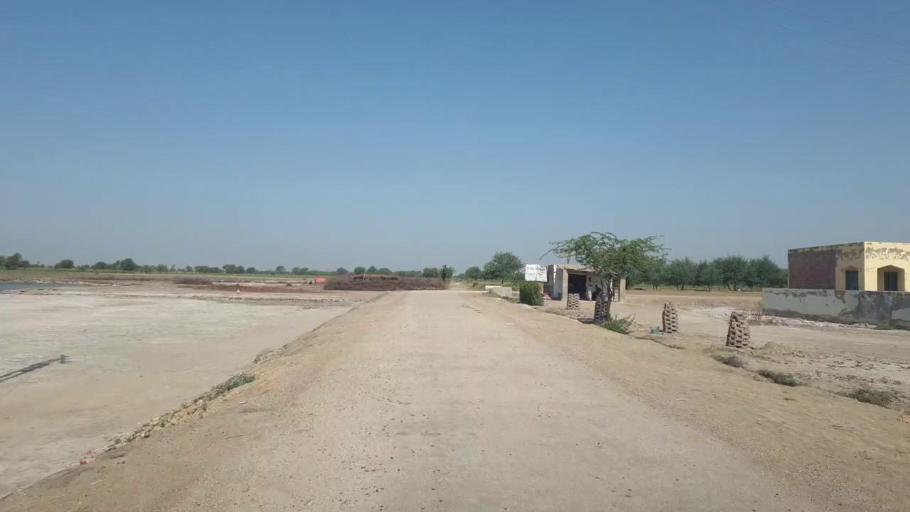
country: PK
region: Sindh
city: Umarkot
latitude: 25.3074
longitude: 69.6133
